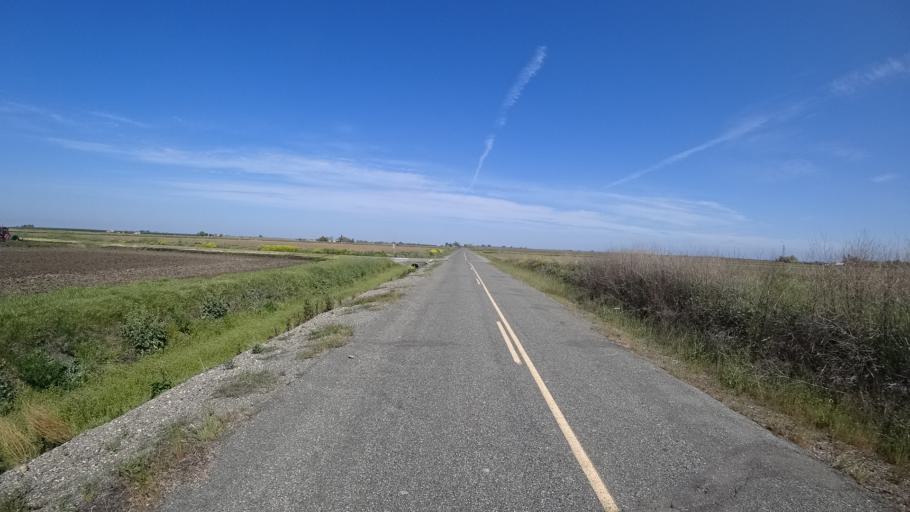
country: US
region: California
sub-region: Glenn County
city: Hamilton City
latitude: 39.6009
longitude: -122.0276
